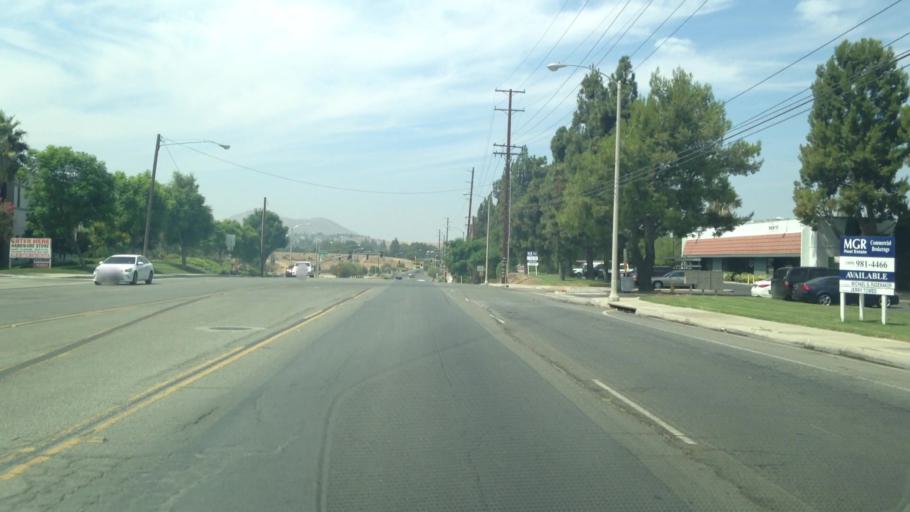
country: US
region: California
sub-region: Riverside County
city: Pedley
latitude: 33.9591
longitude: -117.4589
